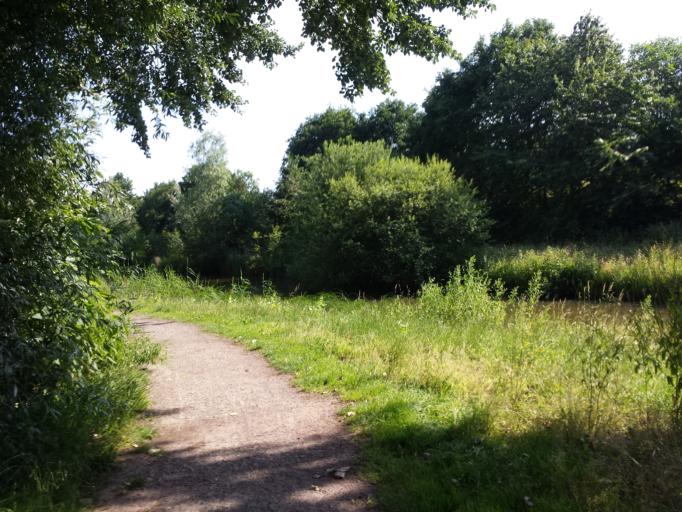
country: DE
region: Lower Saxony
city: Stuhr
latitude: 53.0915
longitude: 8.7446
